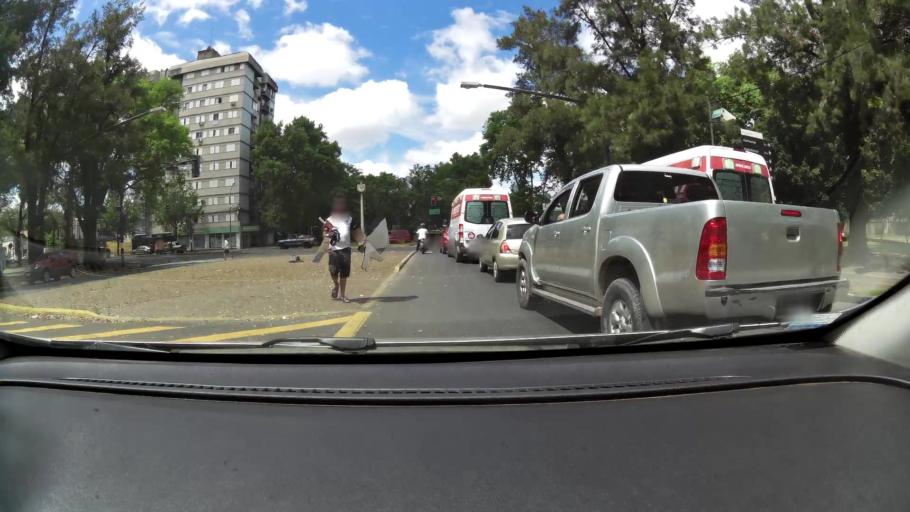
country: AR
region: Santa Fe
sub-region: Departamento de Rosario
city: Rosario
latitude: -32.9646
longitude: -60.6586
